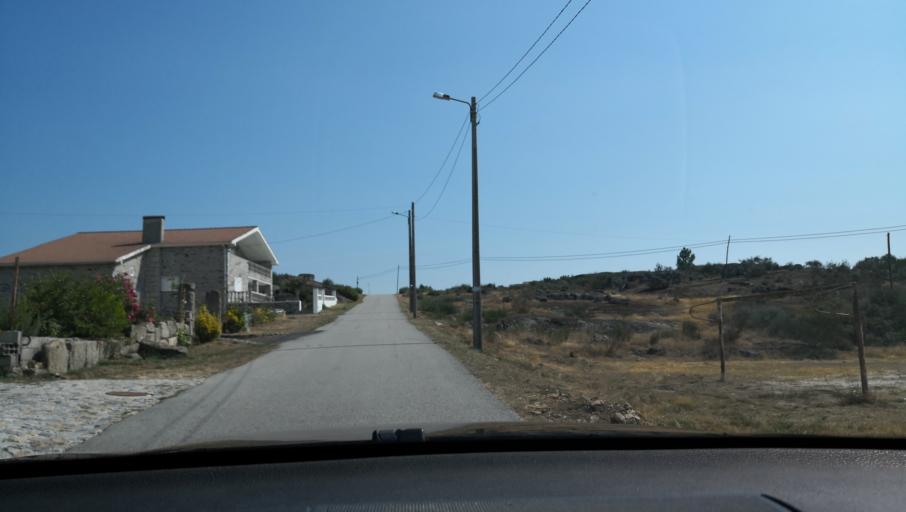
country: PT
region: Vila Real
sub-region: Sabrosa
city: Sabrosa
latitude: 41.2955
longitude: -7.6138
